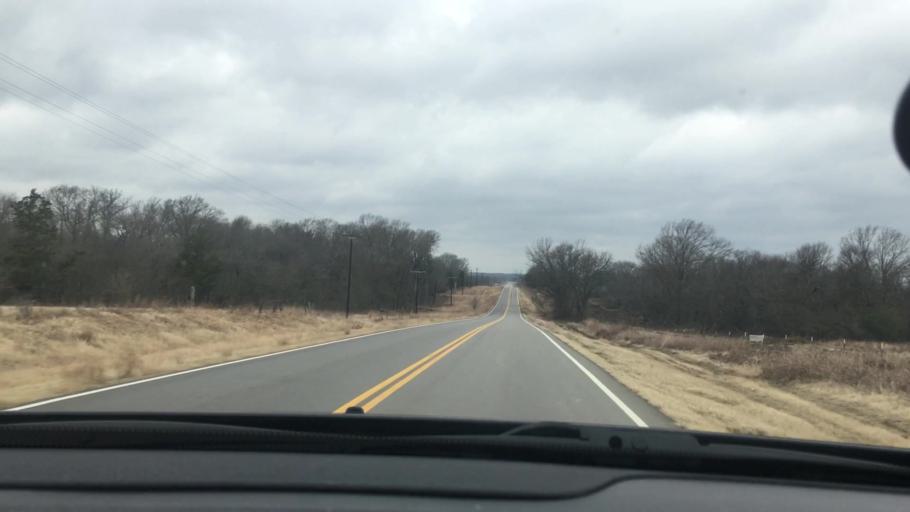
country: US
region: Oklahoma
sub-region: Atoka County
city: Atoka
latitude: 34.3769
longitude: -96.2957
